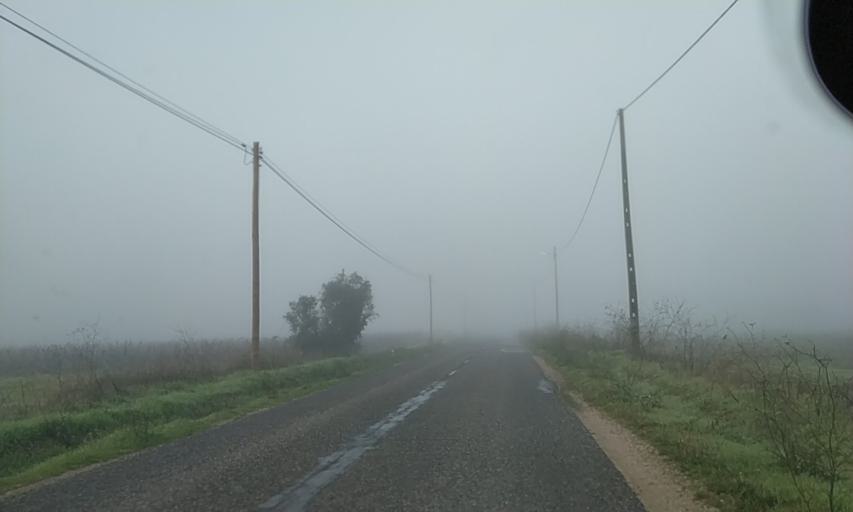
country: PT
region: Setubal
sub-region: Palmela
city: Palmela
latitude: 38.6072
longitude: -8.8517
